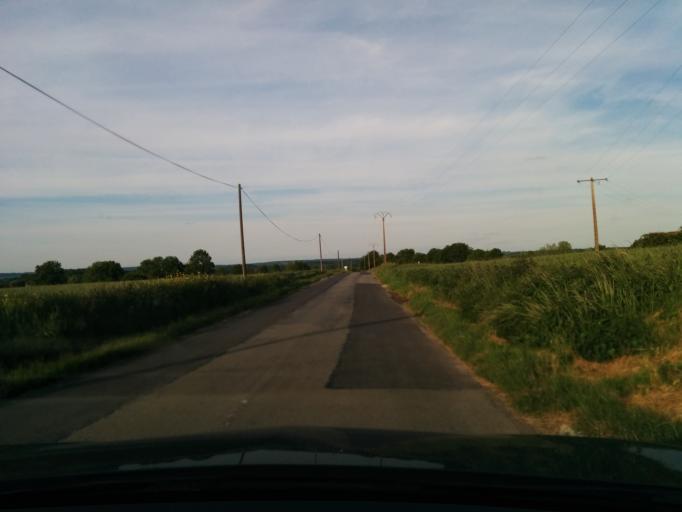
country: FR
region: Haute-Normandie
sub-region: Departement de la Seine-Maritime
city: Neufchatel-en-Bray
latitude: 49.6371
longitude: 1.4420
